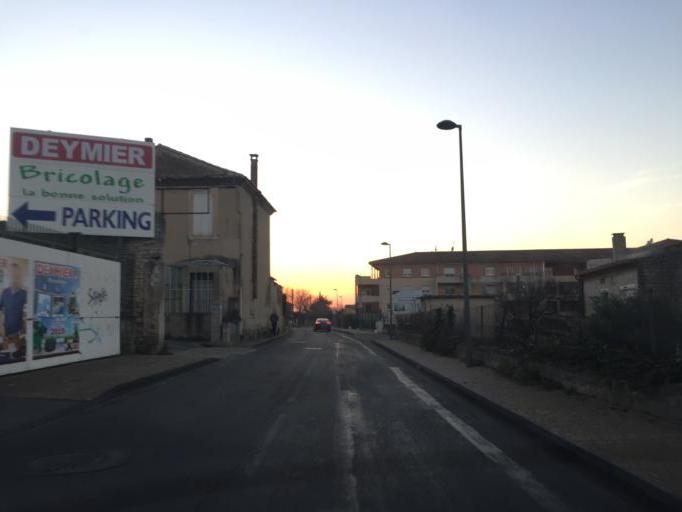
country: FR
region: Provence-Alpes-Cote d'Azur
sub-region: Departement du Vaucluse
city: Carpentras
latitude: 44.0557
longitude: 5.0413
